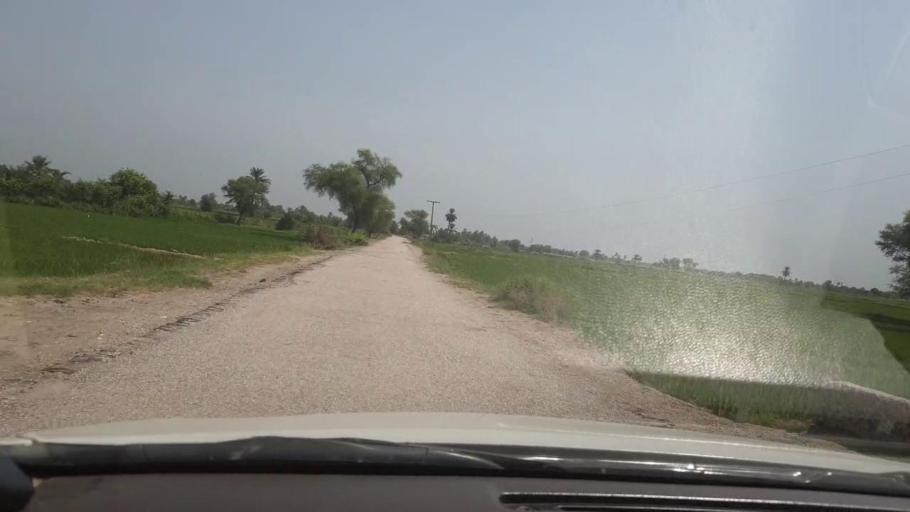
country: PK
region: Sindh
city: Shikarpur
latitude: 27.9400
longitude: 68.5989
